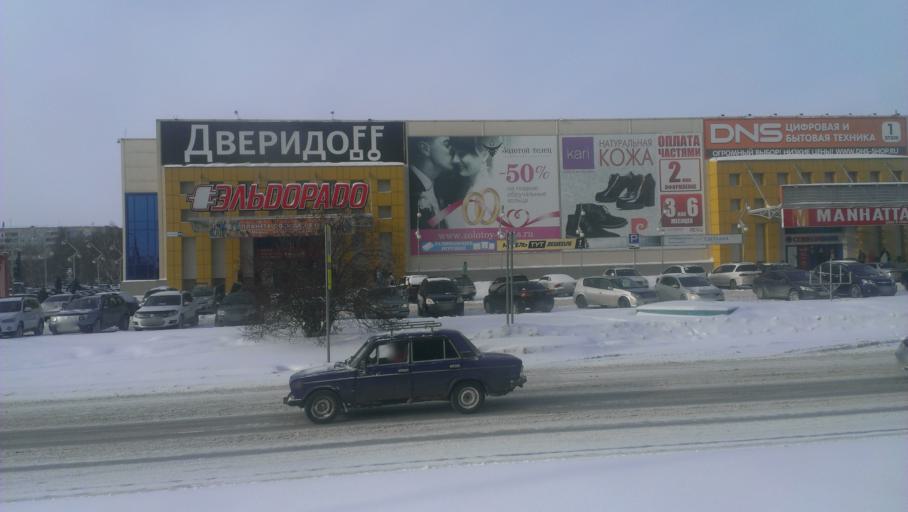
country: RU
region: Altai Krai
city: Novosilikatnyy
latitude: 53.3674
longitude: 83.6768
